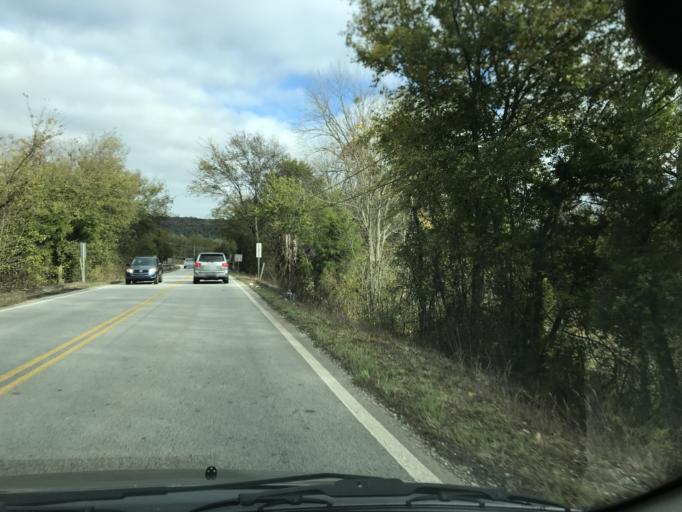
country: US
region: Tennessee
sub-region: Hamilton County
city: Lakesite
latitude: 35.1772
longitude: -85.0382
